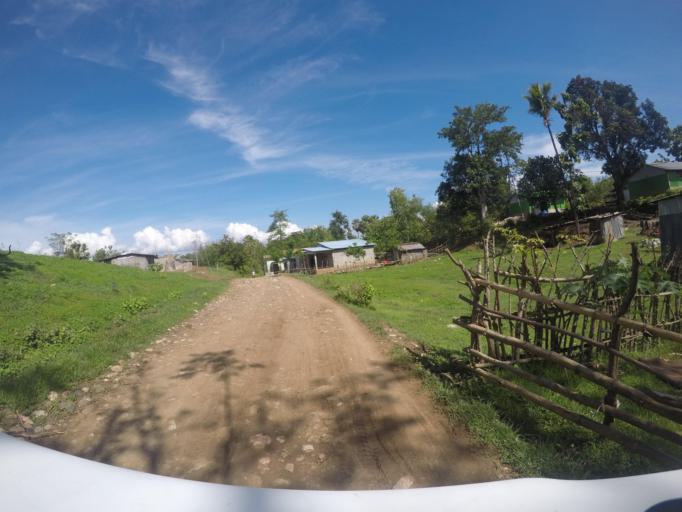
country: TL
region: Bobonaro
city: Maliana
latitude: -8.9848
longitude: 125.1932
